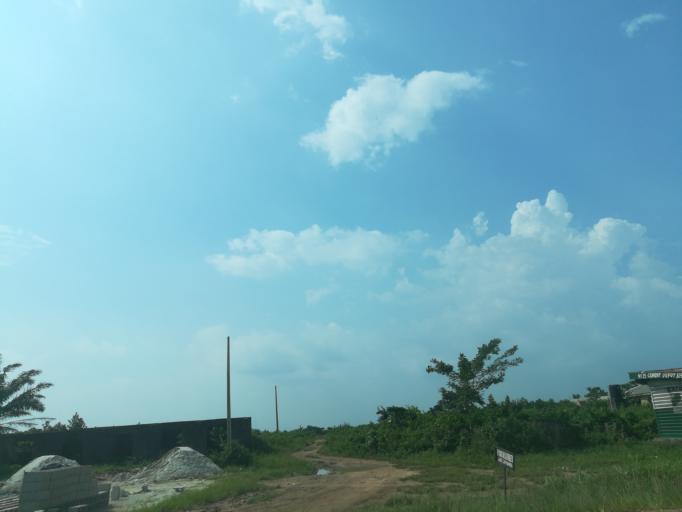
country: NG
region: Lagos
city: Ikorodu
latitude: 6.6180
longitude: 3.6512
